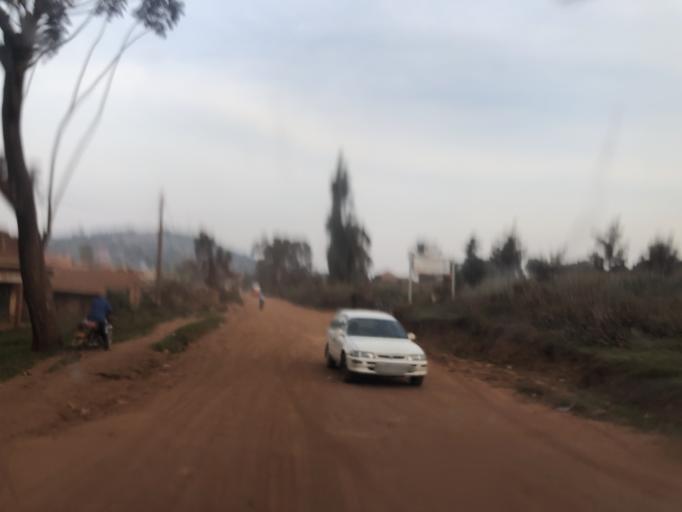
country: UG
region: Central Region
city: Kampala Central Division
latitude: 0.2968
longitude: 32.5195
